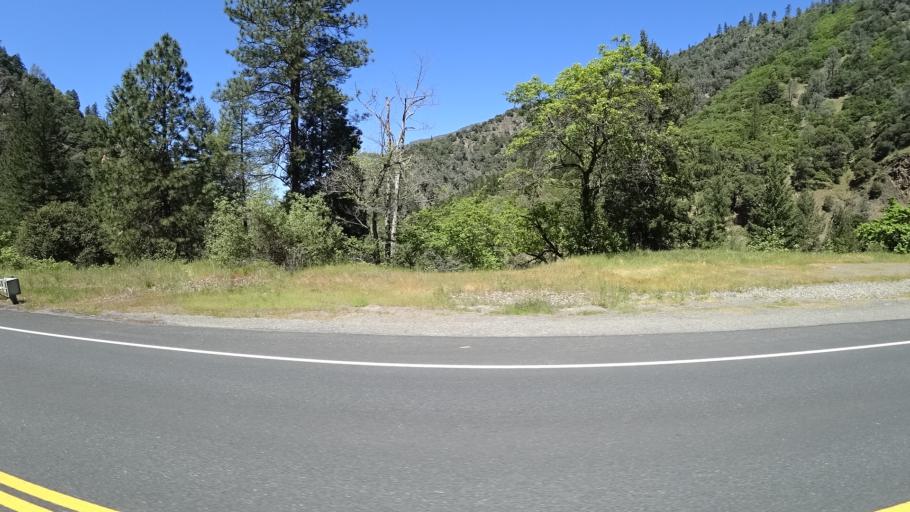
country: US
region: California
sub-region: Humboldt County
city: Willow Creek
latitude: 40.7902
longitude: -123.4534
